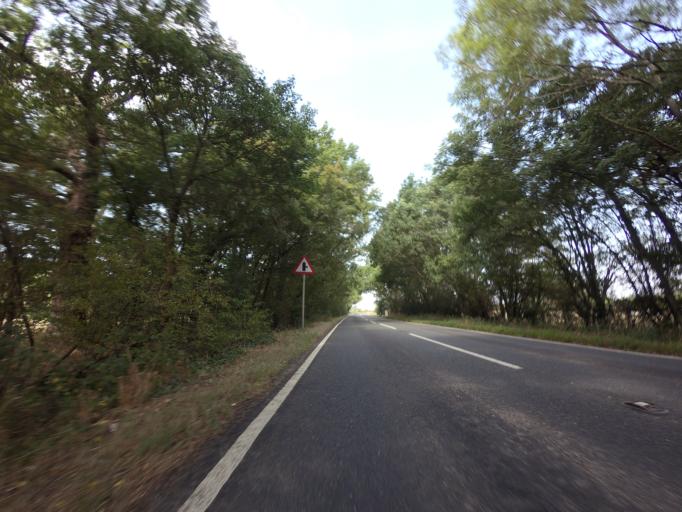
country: GB
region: England
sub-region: Kent
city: Headcorn
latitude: 51.1157
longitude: 0.6216
